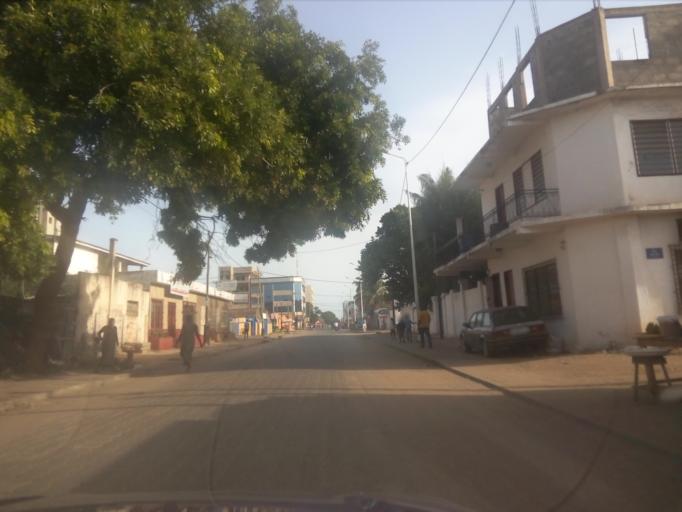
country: TG
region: Maritime
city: Lome
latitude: 6.1390
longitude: 1.2280
